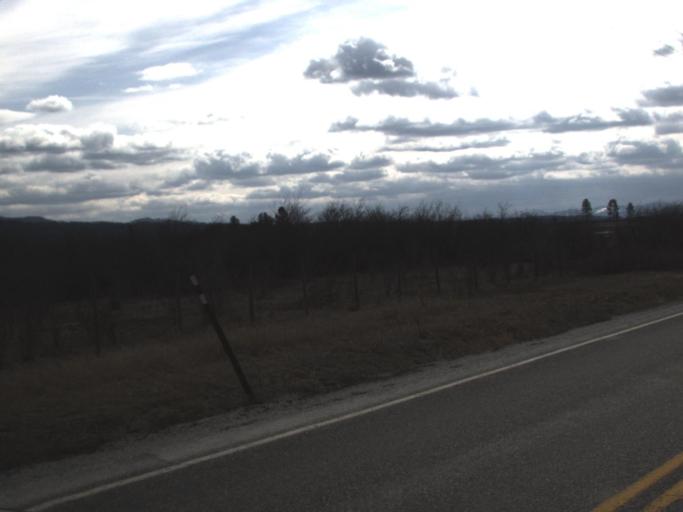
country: US
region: Washington
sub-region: Pend Oreille County
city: Newport
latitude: 48.3737
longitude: -117.3048
